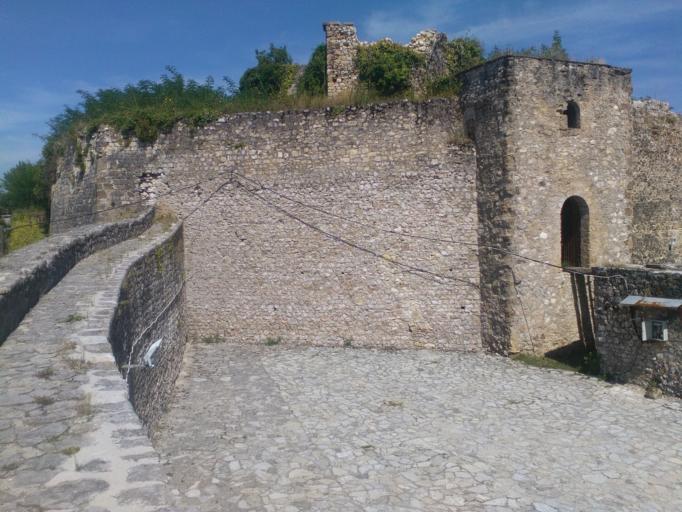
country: BA
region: Federation of Bosnia and Herzegovina
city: Ostrozac
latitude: 44.9057
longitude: 15.9367
